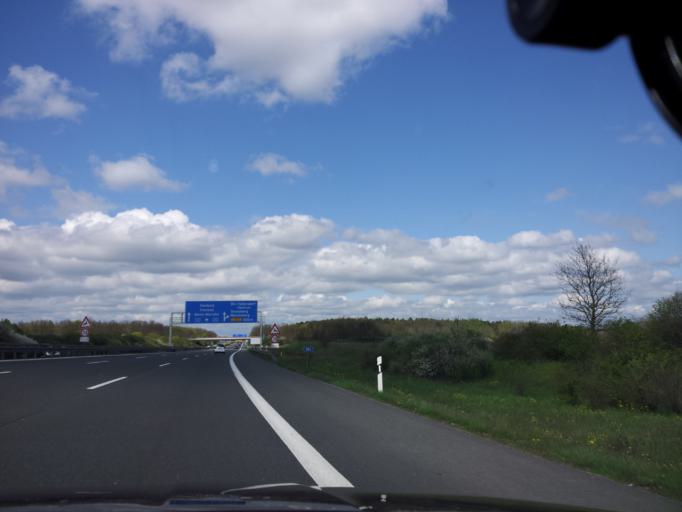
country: DE
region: Brandenburg
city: Woltersdorf
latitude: 52.4823
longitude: 13.7548
